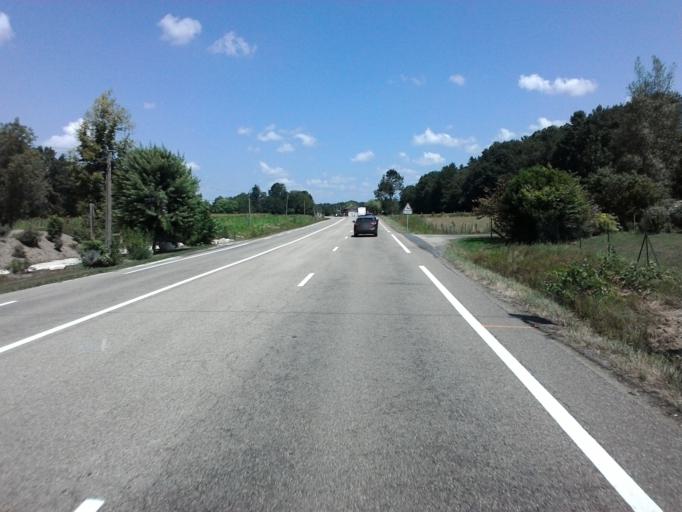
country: FR
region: Rhone-Alpes
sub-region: Departement de l'Ain
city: Saint-Etienne-du-Bois
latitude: 46.2483
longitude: 5.2722
